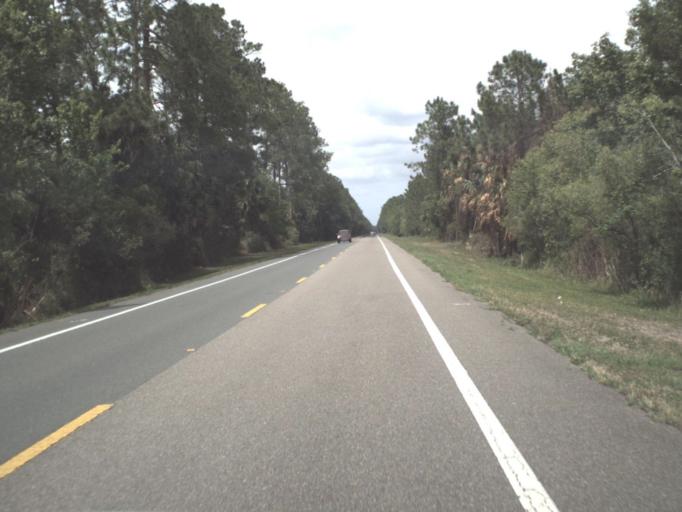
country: US
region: Florida
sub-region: Flagler County
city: Bunnell
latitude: 29.3824
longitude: -81.3099
